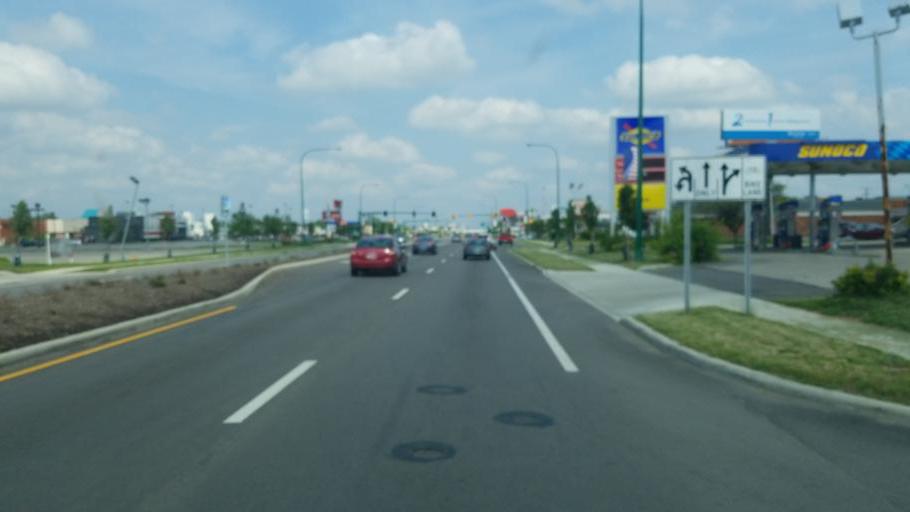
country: US
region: Ohio
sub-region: Franklin County
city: Lincoln Village
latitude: 39.9520
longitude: -83.1314
